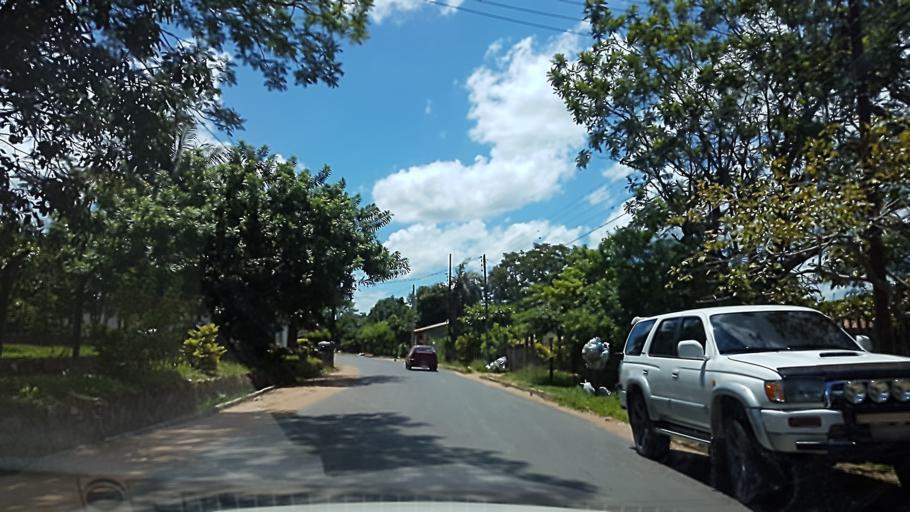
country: PY
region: Central
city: Colonia Mariano Roque Alonso
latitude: -25.2383
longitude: -57.5291
